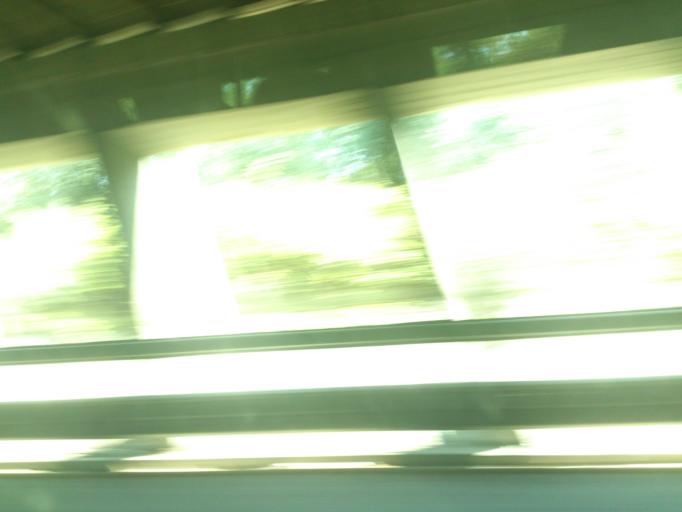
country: IT
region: Calabria
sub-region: Provincia di Vibo-Valentia
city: Francavilla Angitola
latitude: 38.7999
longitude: 16.2286
